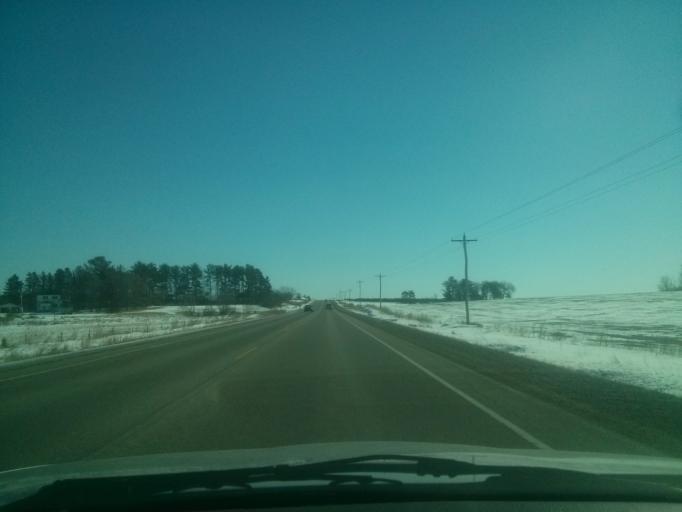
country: US
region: Wisconsin
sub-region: Saint Croix County
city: New Richmond
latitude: 45.1369
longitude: -92.4457
